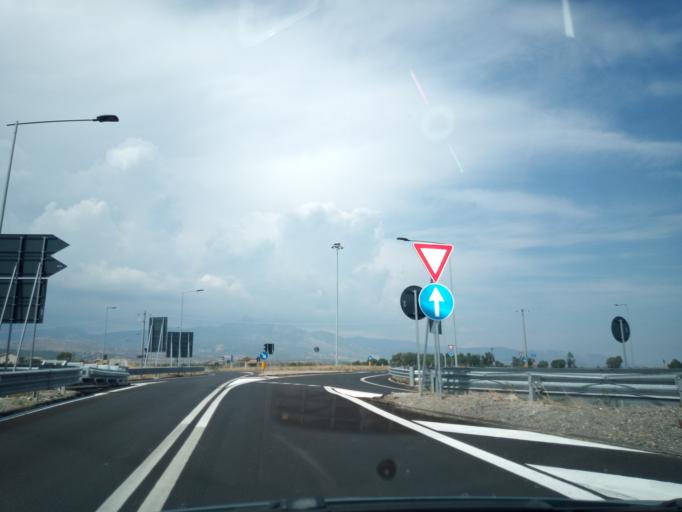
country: IT
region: Calabria
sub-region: Provincia di Cosenza
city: Doria
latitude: 39.7238
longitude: 16.3644
